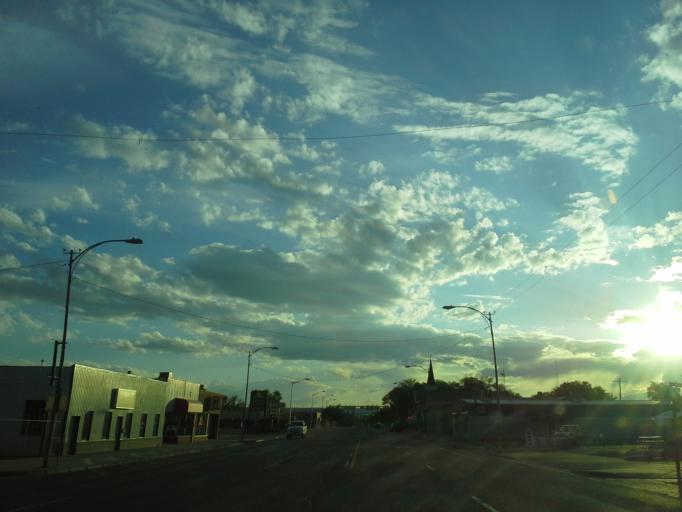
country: US
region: Wyoming
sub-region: Washakie County
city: Worland
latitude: 44.0169
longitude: -107.9515
